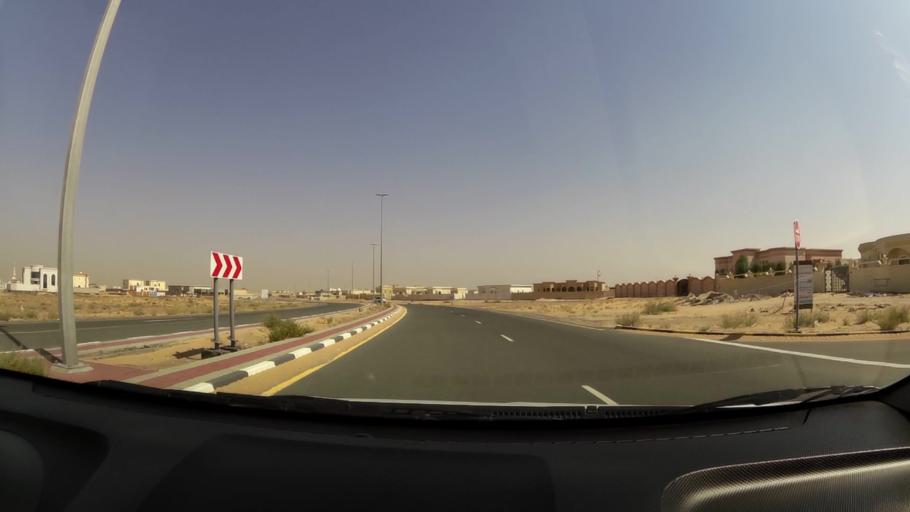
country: AE
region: Umm al Qaywayn
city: Umm al Qaywayn
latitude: 25.4770
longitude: 55.6048
